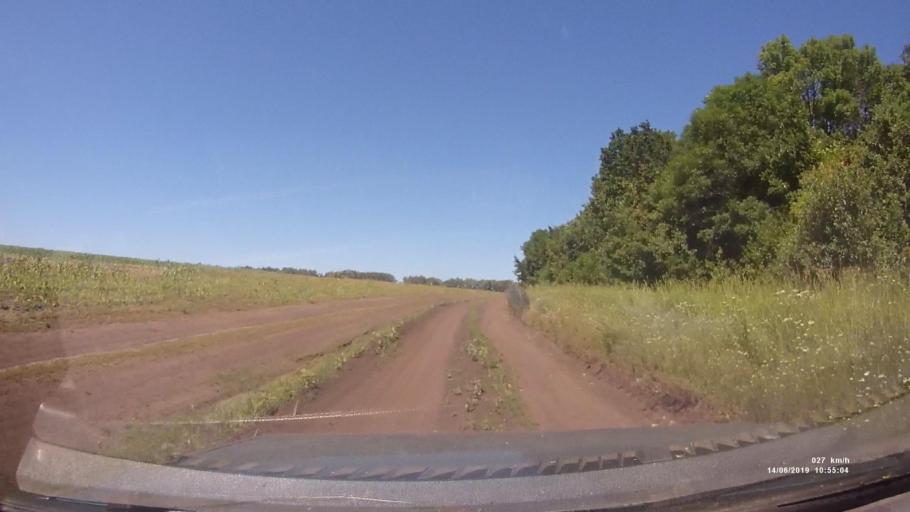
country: RU
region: Rostov
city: Kazanskaya
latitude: 49.8625
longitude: 41.3739
